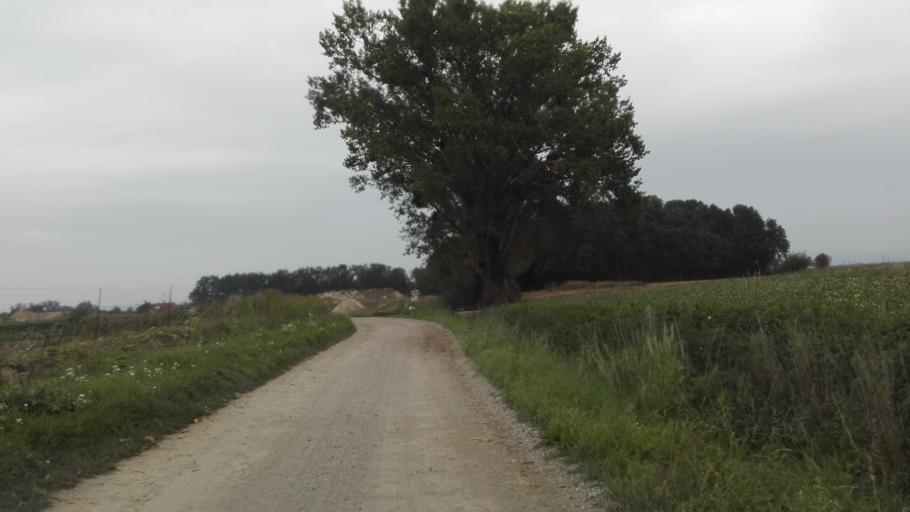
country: AT
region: Upper Austria
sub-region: Politischer Bezirk Urfahr-Umgebung
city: Feldkirchen an der Donau
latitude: 48.2848
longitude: 14.0537
